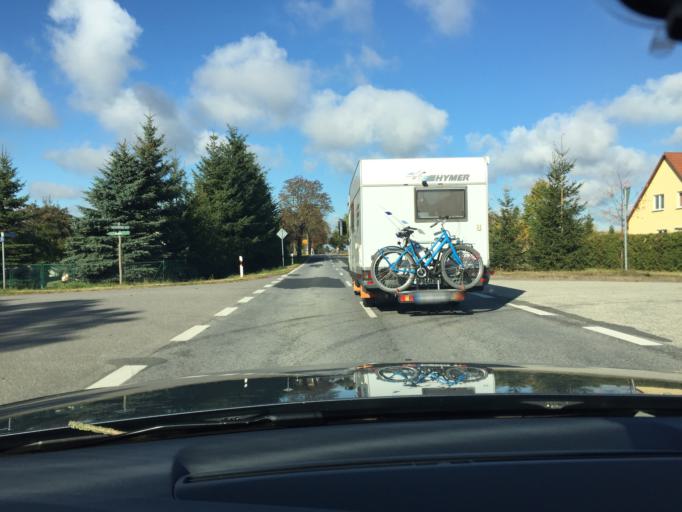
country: DE
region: Mecklenburg-Vorpommern
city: Lalendorf
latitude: 53.6870
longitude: 12.3569
